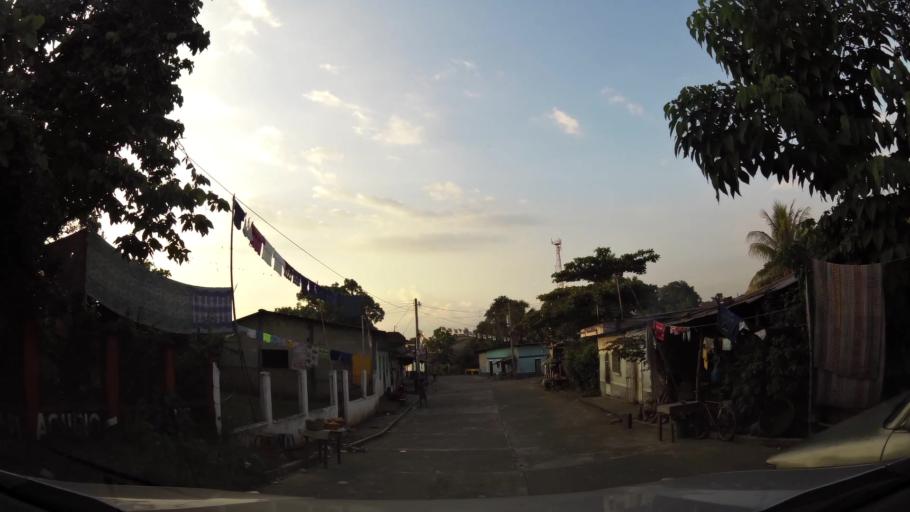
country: GT
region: Retalhuleu
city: San Sebastian
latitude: 14.5583
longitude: -91.6470
